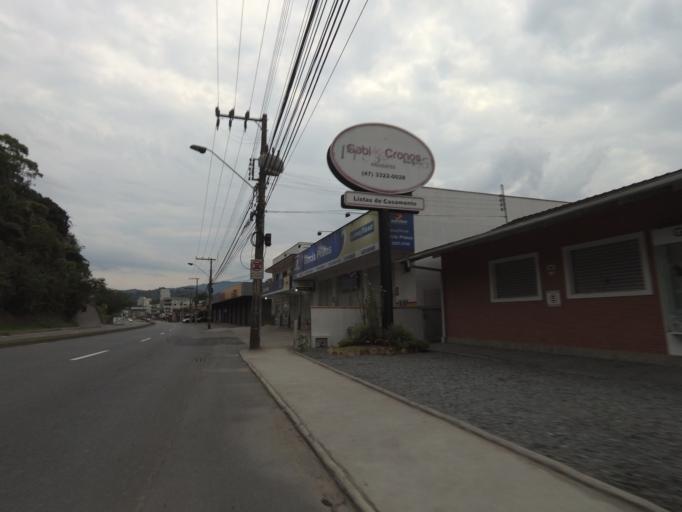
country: BR
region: Santa Catarina
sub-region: Blumenau
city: Blumenau
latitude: -26.9047
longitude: -49.0653
